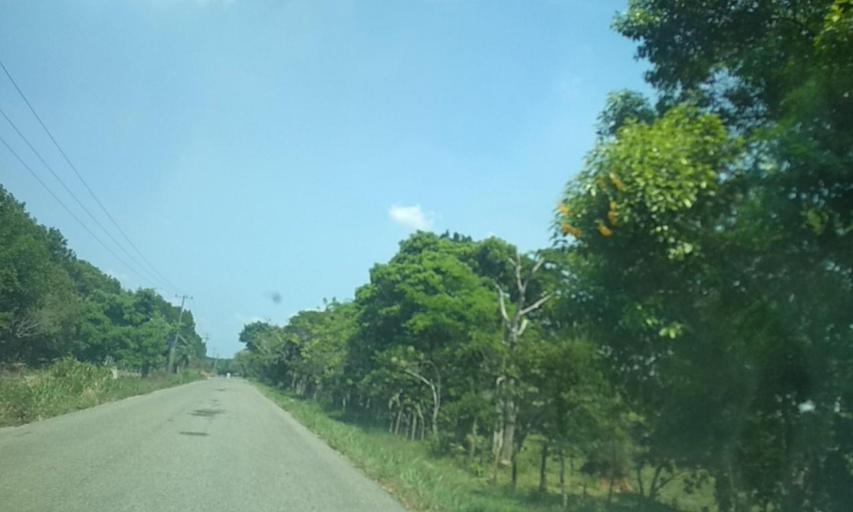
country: MX
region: Tabasco
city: Huimanguillo
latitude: 17.8004
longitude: -93.4743
